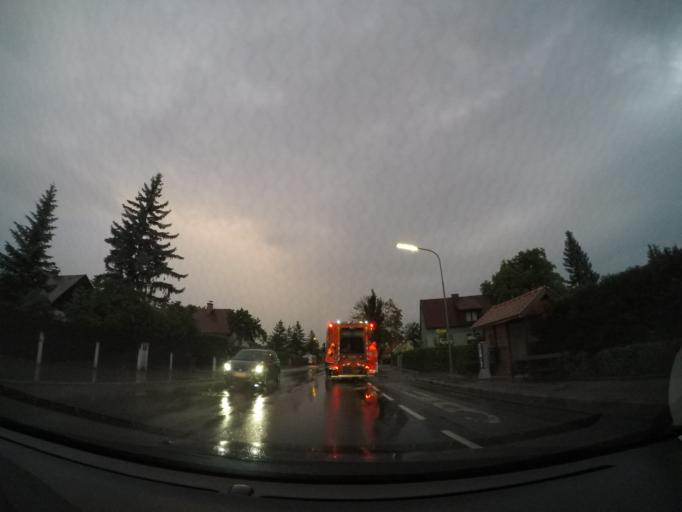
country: AT
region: Lower Austria
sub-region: Politischer Bezirk Baden
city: Bad Voslau
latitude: 47.9597
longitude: 16.2172
